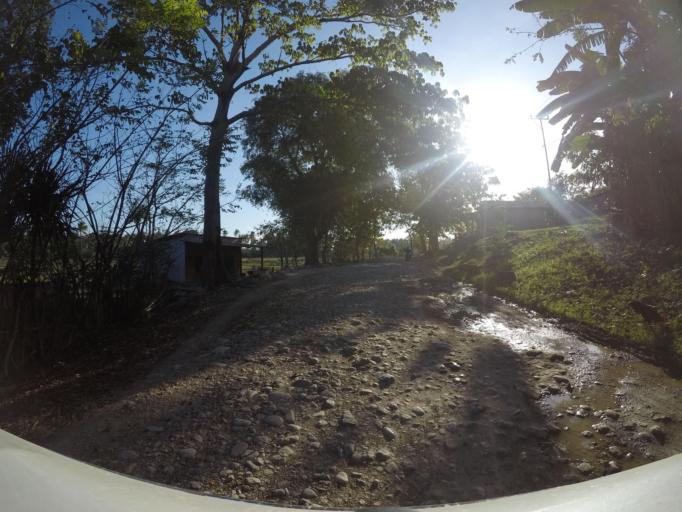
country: TL
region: Viqueque
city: Viqueque
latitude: -8.8049
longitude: 126.5747
